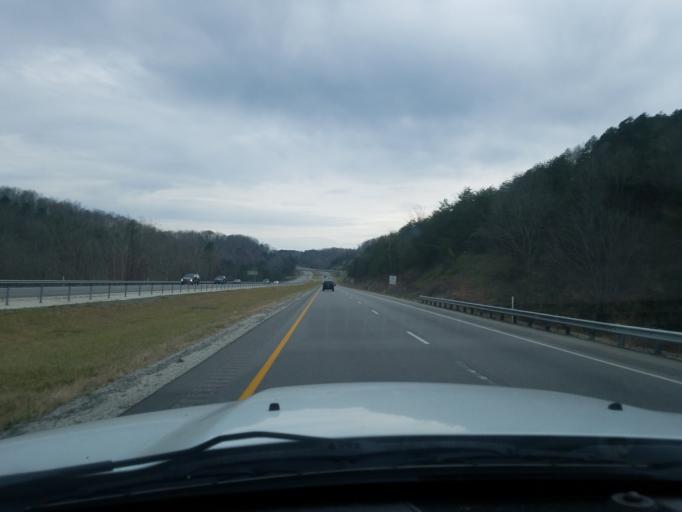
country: US
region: Kentucky
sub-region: Carter County
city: Grayson
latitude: 38.3714
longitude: -82.8320
